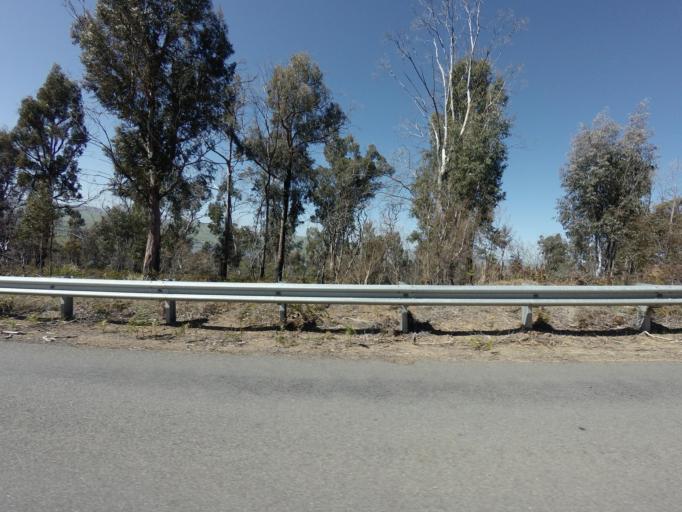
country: AU
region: Tasmania
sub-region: Derwent Valley
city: New Norfolk
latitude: -42.5490
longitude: 146.7143
